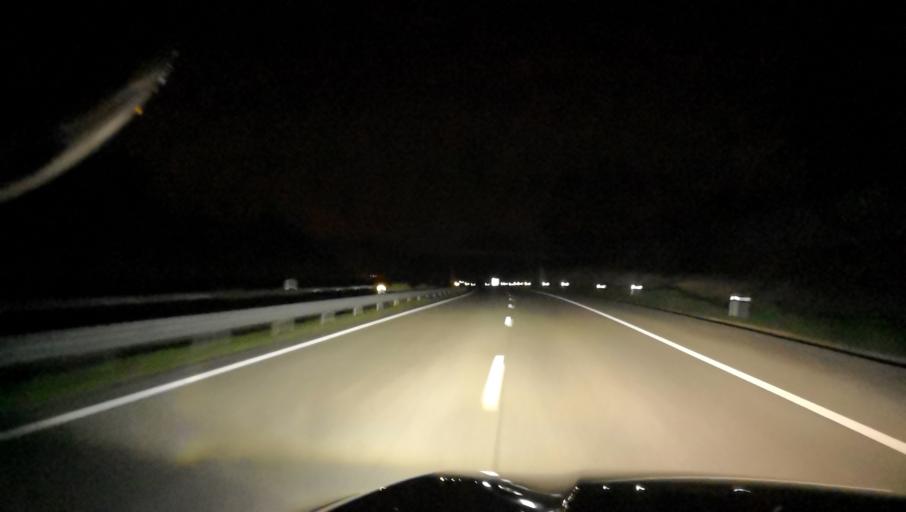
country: PT
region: Viseu
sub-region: Oliveira de Frades
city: Oliveira de Frades
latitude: 40.6825
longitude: -8.1855
